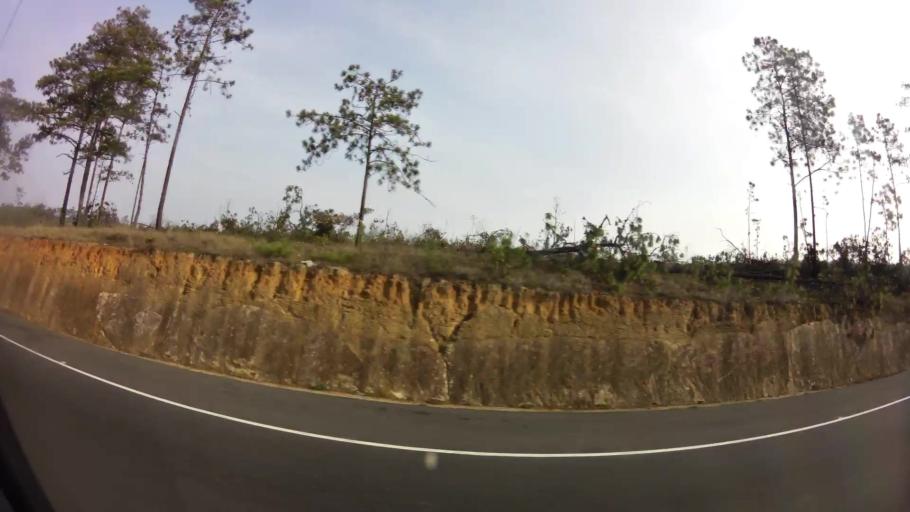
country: HN
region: Francisco Morazan
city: Zambrano
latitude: 14.2897
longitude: -87.4420
